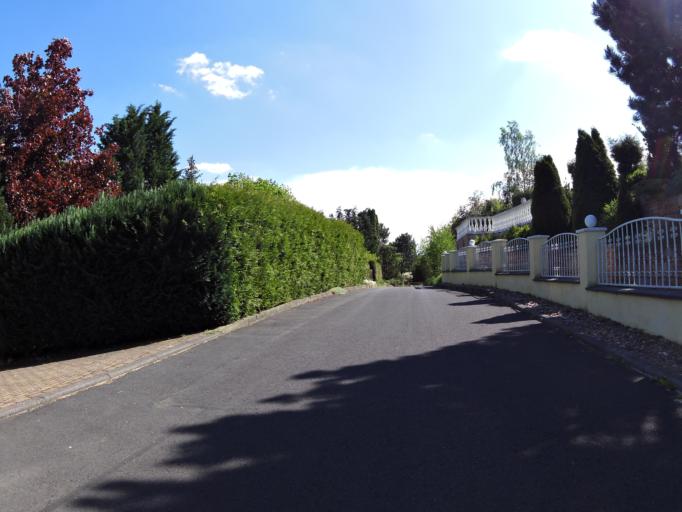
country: DE
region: Thuringia
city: Leimbach
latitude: 50.8088
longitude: 10.2100
